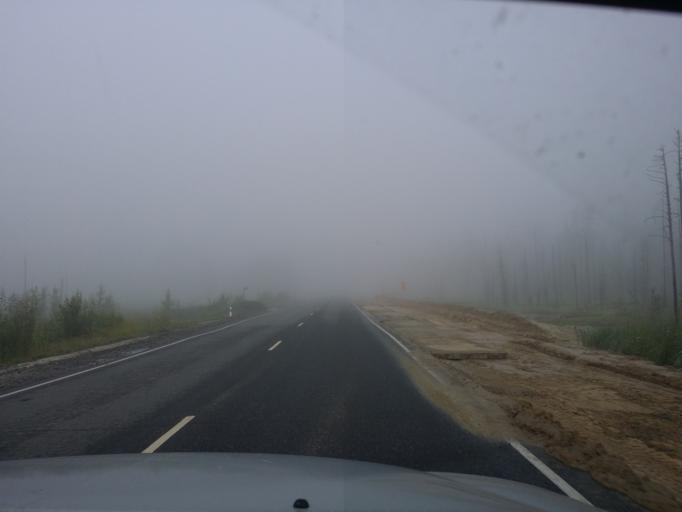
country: RU
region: Khanty-Mansiyskiy Avtonomnyy Okrug
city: Gornopravdinsk
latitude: 59.6525
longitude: 69.9258
